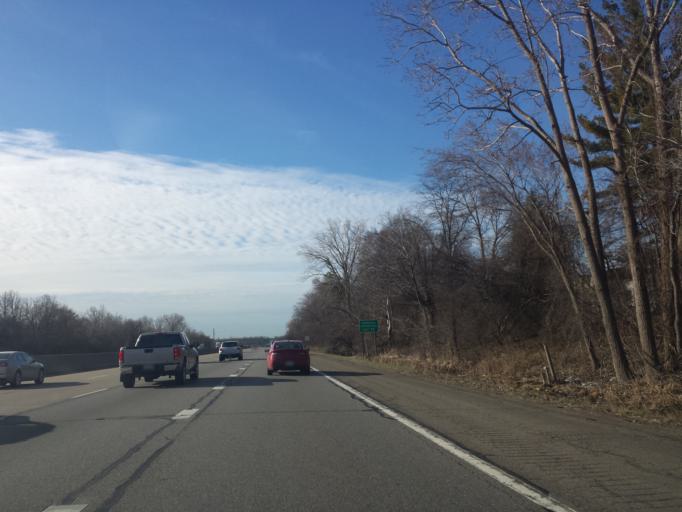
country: US
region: Michigan
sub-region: Oakland County
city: Bloomfield Hills
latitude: 42.6272
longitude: -83.2379
